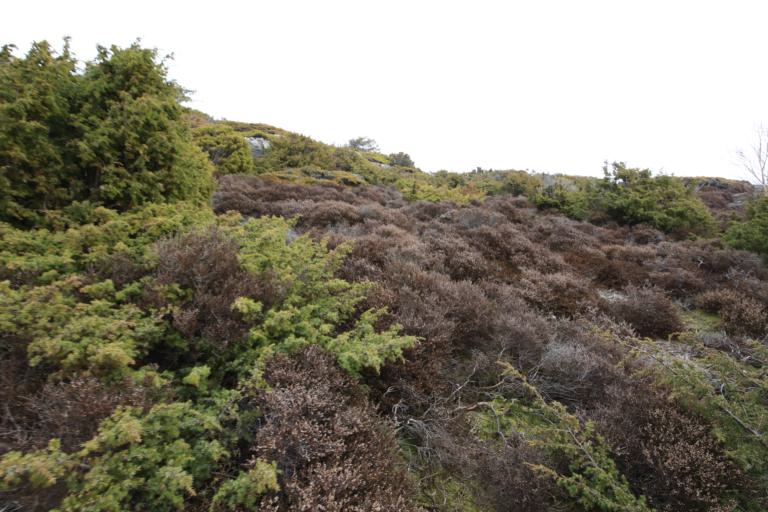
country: SE
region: Halland
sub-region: Kungsbacka Kommun
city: Frillesas
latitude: 57.2480
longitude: 12.1009
